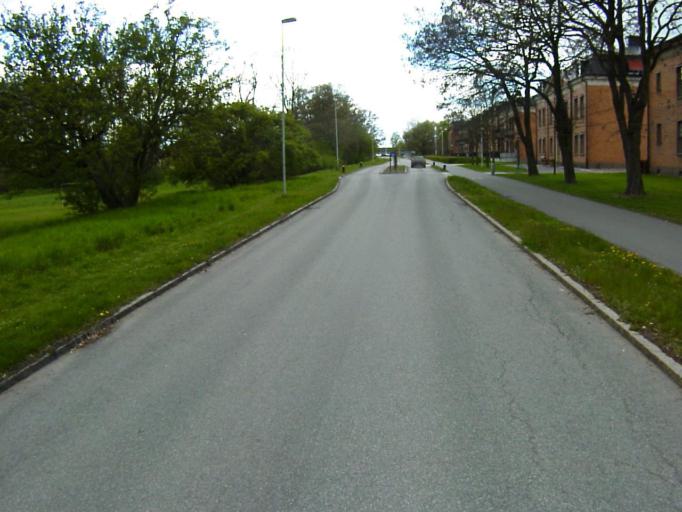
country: SE
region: Skane
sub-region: Kristianstads Kommun
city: Kristianstad
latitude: 56.0368
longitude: 14.1574
